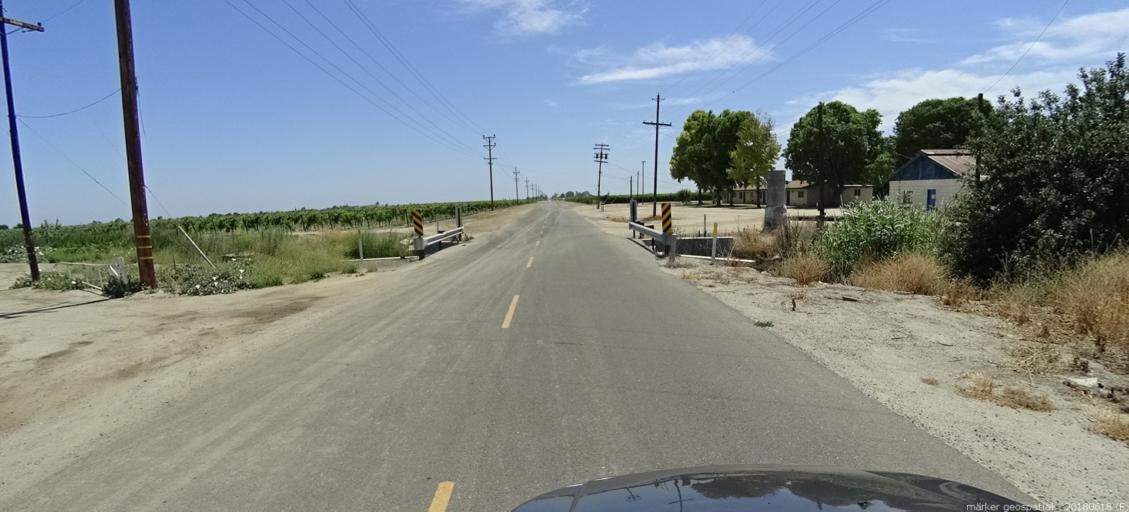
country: US
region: California
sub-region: Madera County
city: Parkwood
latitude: 36.8803
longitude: -120.1481
